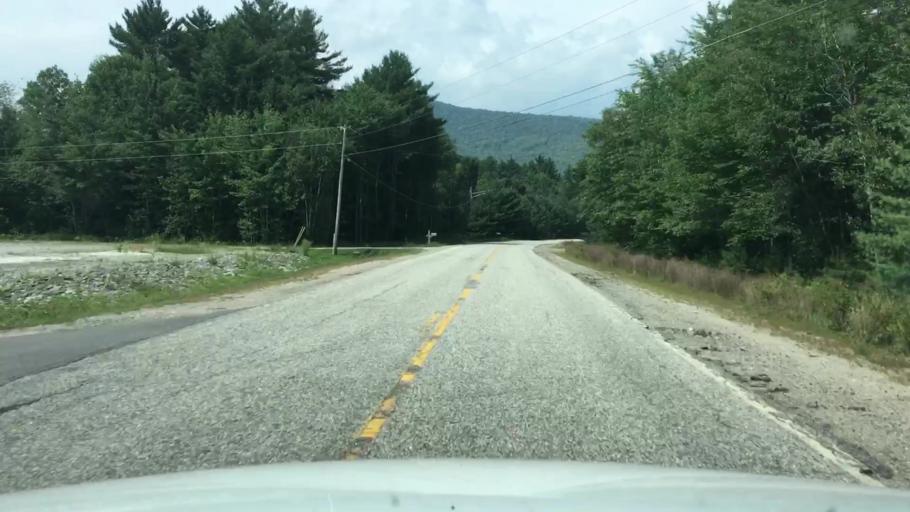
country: US
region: Maine
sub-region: Oxford County
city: Rumford
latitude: 44.5790
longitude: -70.7313
